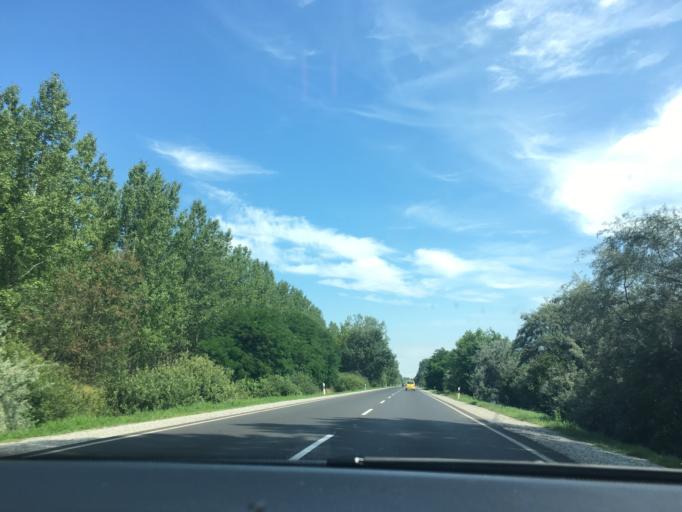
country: HU
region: Szabolcs-Szatmar-Bereg
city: Ujfeherto
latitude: 47.8397
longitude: 21.7047
